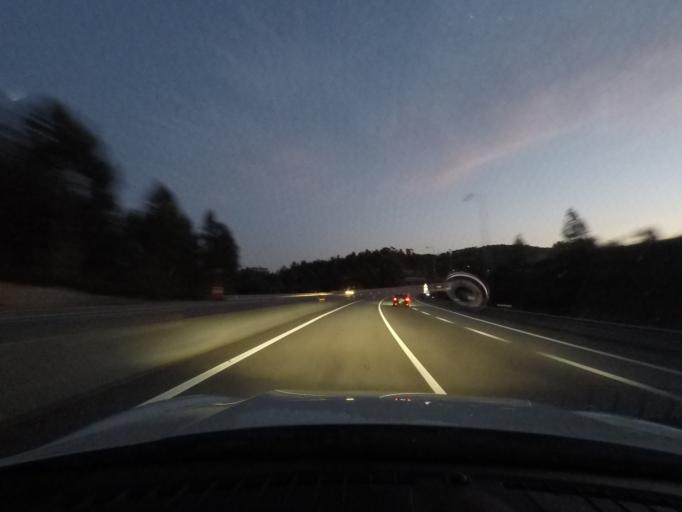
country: PT
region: Porto
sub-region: Vila Nova de Gaia
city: Sandim
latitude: 41.0315
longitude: -8.4949
